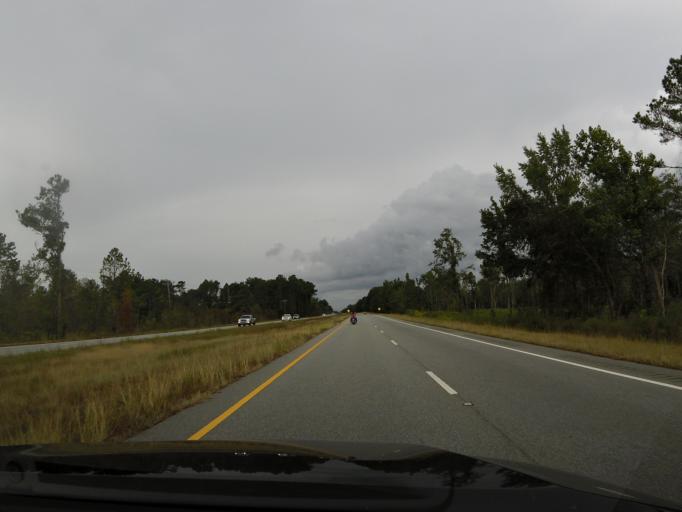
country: US
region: Georgia
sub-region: McIntosh County
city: Darien
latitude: 31.3691
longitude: -81.6241
